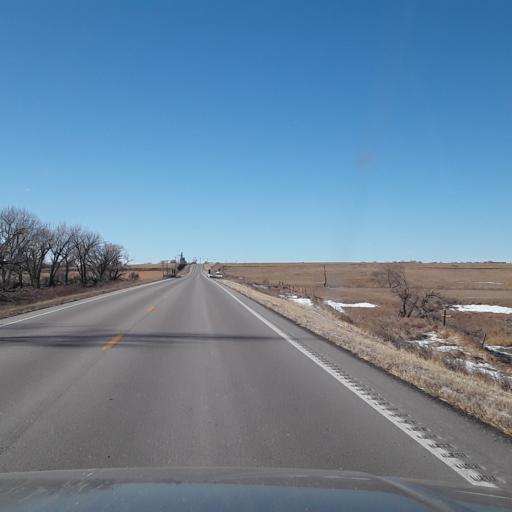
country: US
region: Nebraska
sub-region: Dawson County
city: Gothenburg
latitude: 40.7039
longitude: -100.1881
